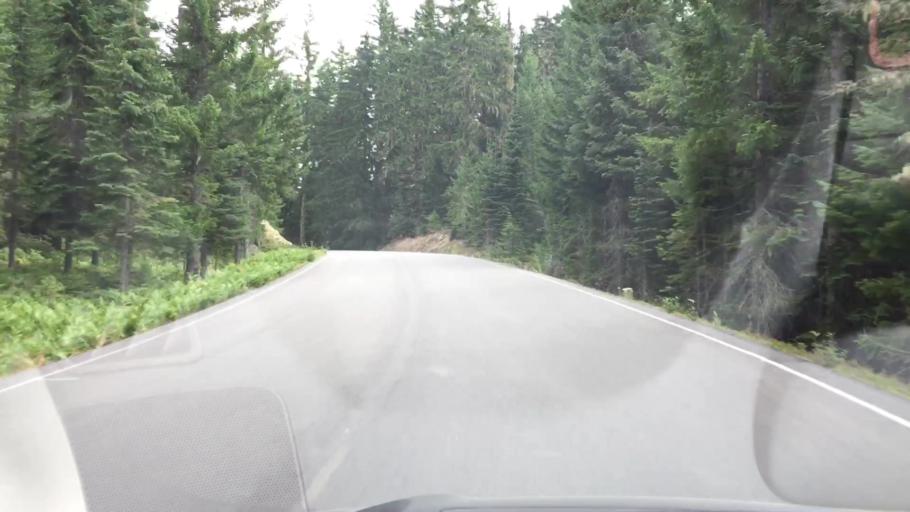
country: US
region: Washington
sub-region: Klickitat County
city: White Salmon
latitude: 46.1898
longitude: -121.6490
